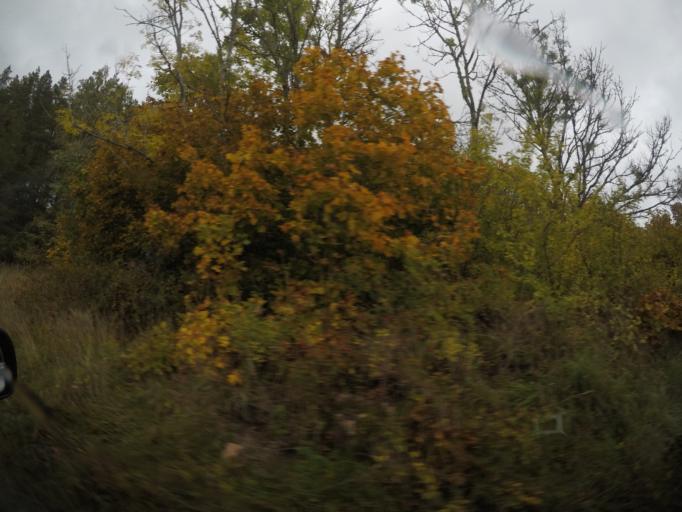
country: SE
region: Soedermanland
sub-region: Eskilstuna Kommun
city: Kvicksund
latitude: 59.3305
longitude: 16.2978
